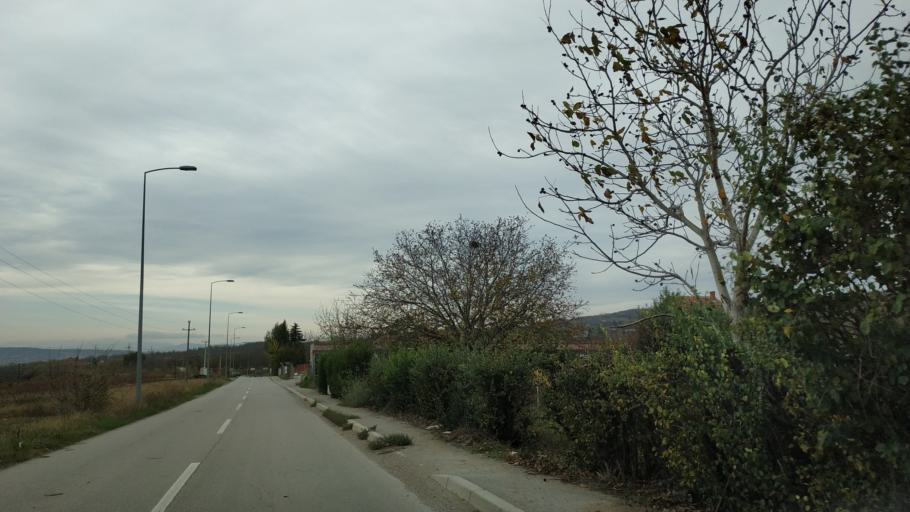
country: RS
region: Central Serbia
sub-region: Nisavski Okrug
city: Nis
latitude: 43.3536
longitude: 21.9446
